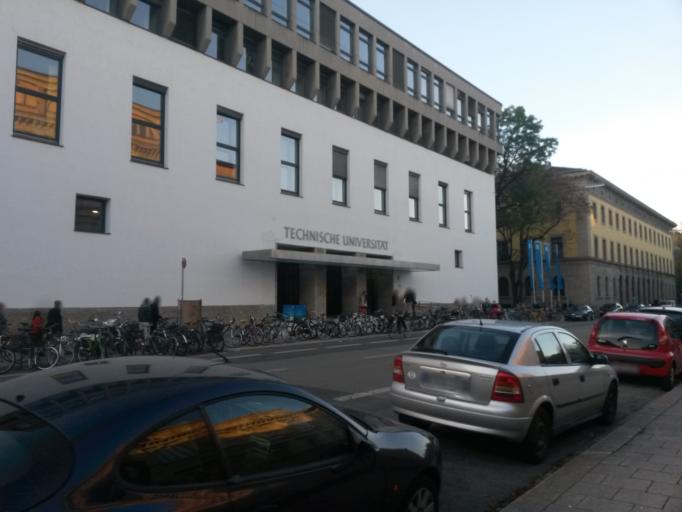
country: DE
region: Bavaria
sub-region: Upper Bavaria
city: Munich
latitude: 48.1484
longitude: 11.5687
